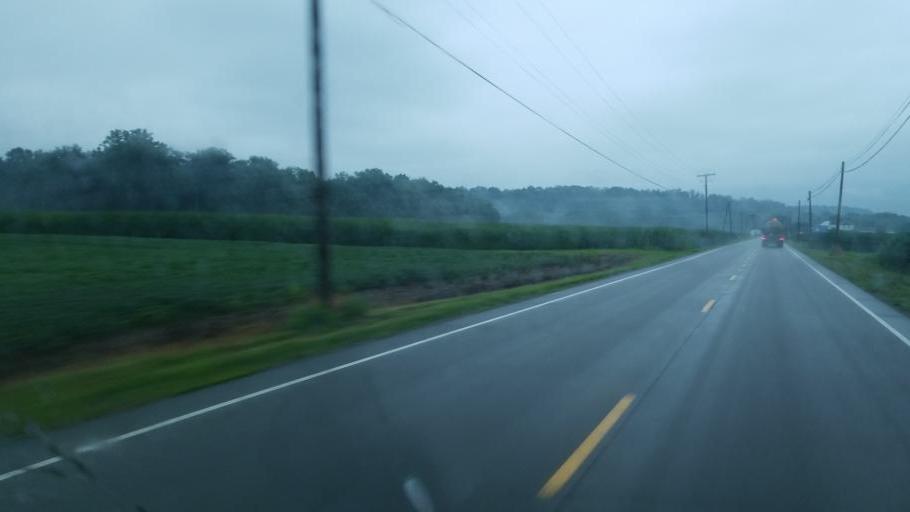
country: US
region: Ohio
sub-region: Coshocton County
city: Coshocton
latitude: 40.3337
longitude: -81.9517
